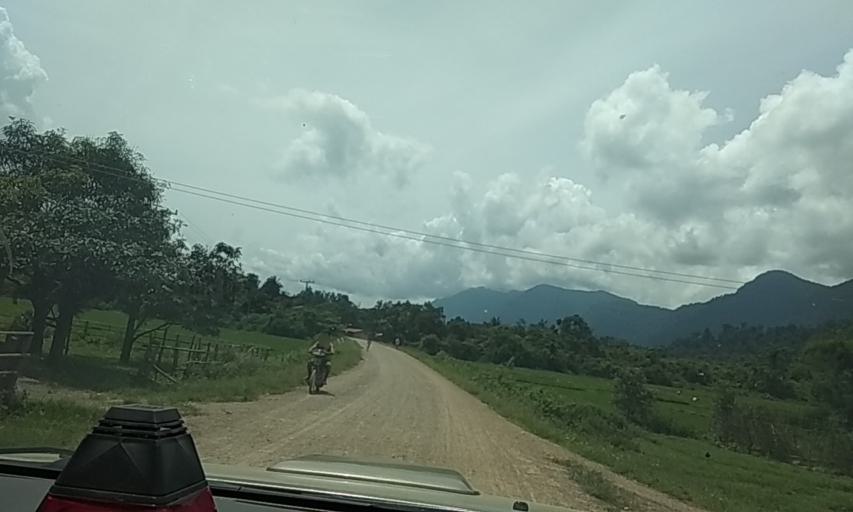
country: LA
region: Bolikhamxai
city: Ban Nahin
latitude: 18.1528
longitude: 104.7234
